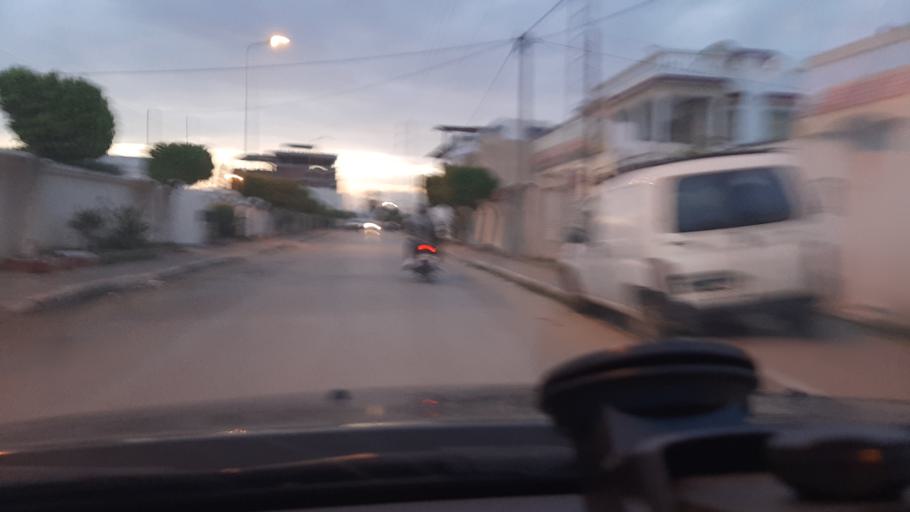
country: TN
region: Safaqis
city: Sfax
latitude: 34.7636
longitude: 10.6947
